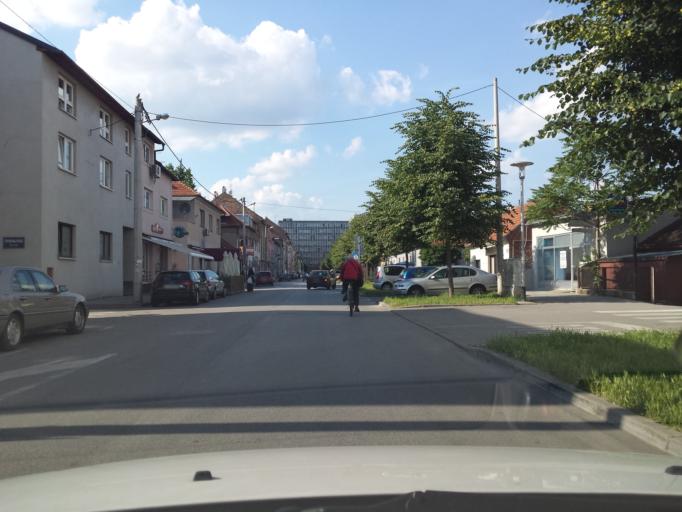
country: HR
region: Grad Zagreb
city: Novi Zagreb
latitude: 45.7964
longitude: 15.9805
